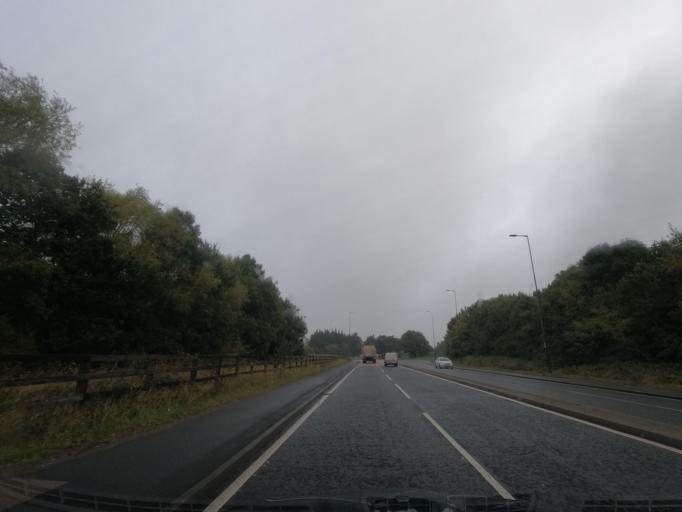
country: GB
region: England
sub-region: Redcar and Cleveland
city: South Bank
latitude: 54.5865
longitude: -1.1335
